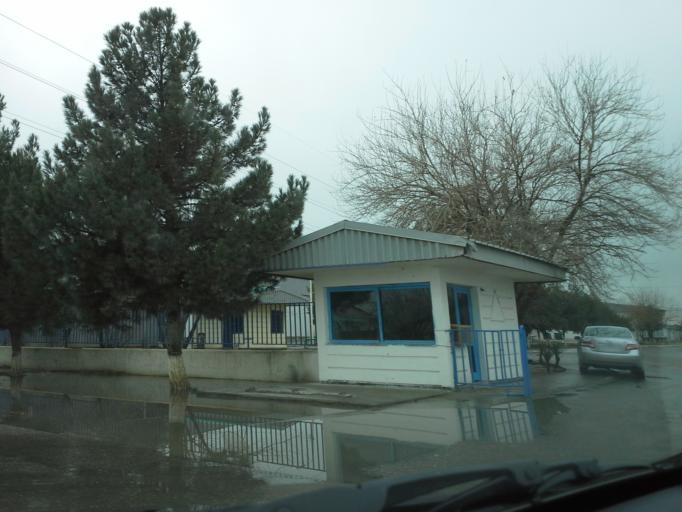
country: TM
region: Ahal
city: Ashgabat
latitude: 37.9476
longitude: 58.4339
